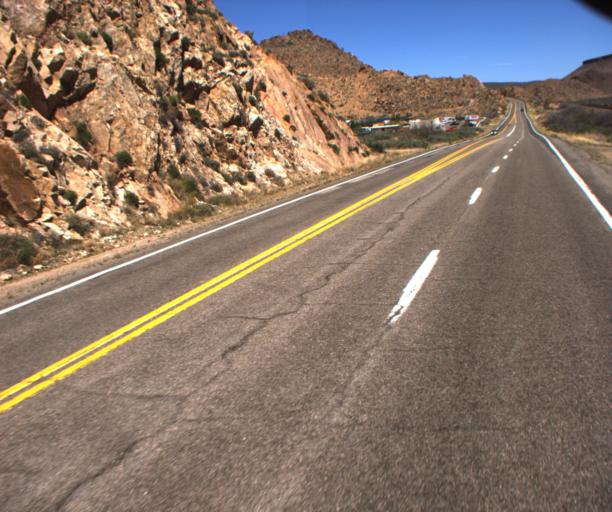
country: US
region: Arizona
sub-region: Mohave County
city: Peach Springs
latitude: 35.4060
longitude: -113.6502
